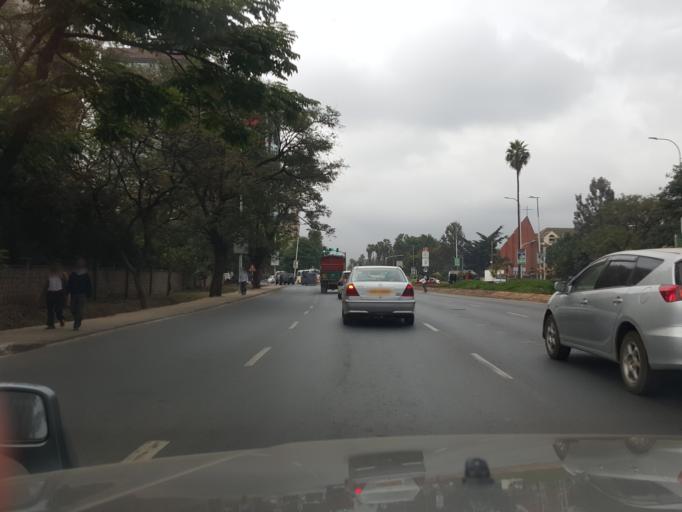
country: KE
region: Nairobi Area
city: Nairobi
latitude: -1.2805
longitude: 36.8145
